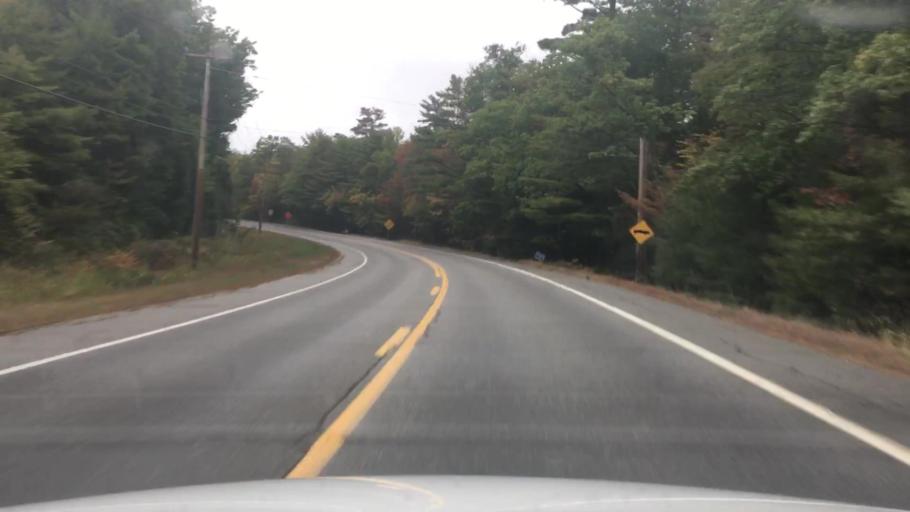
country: US
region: Maine
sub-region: Kennebec County
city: Rome
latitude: 44.5210
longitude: -69.8795
